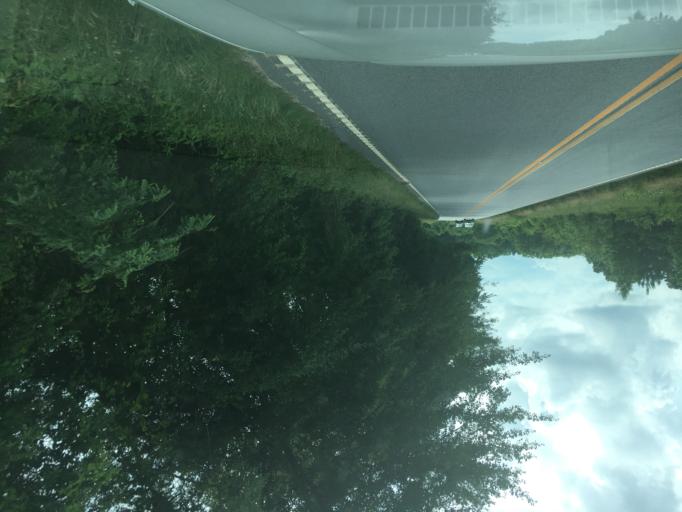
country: US
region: South Carolina
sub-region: Laurens County
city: Watts Mills
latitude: 34.5324
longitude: -81.9652
